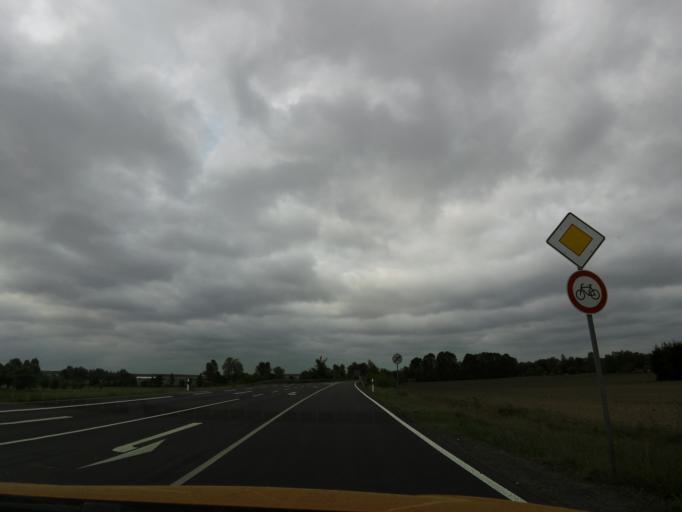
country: DE
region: Brandenburg
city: Beelitz
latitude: 52.2341
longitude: 12.9872
